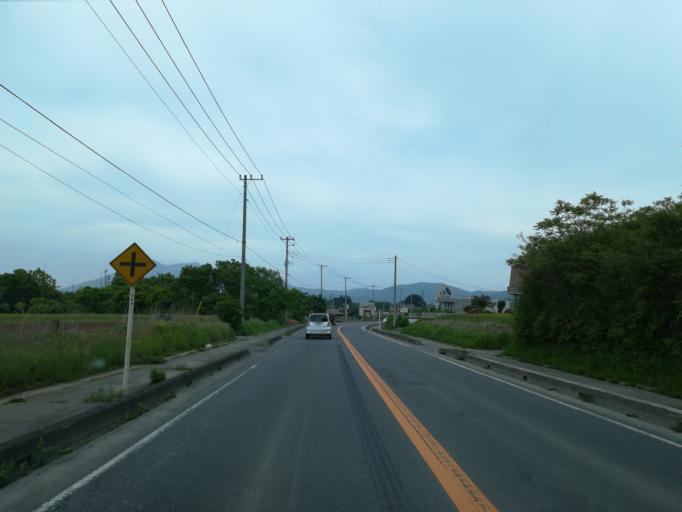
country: JP
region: Ibaraki
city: Tsukuba
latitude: 36.1409
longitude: 140.0847
